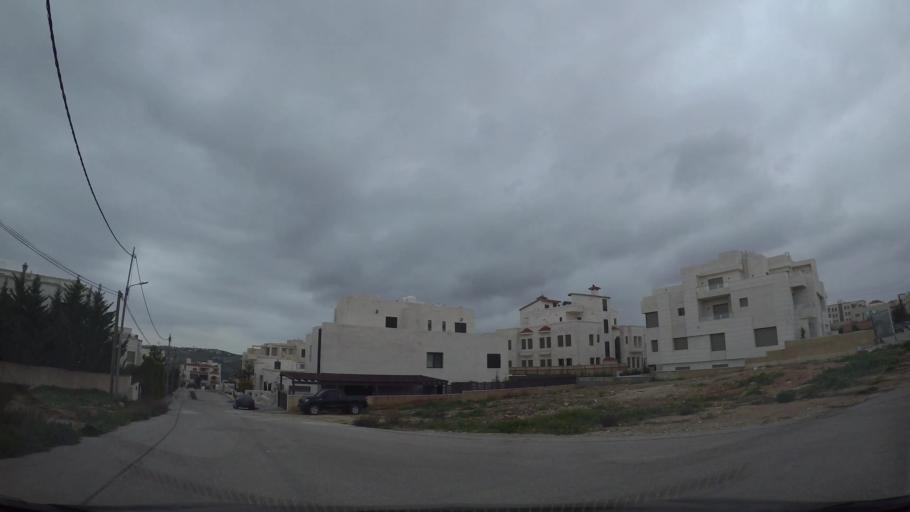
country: JO
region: Amman
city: Wadi as Sir
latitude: 31.9609
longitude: 35.8253
